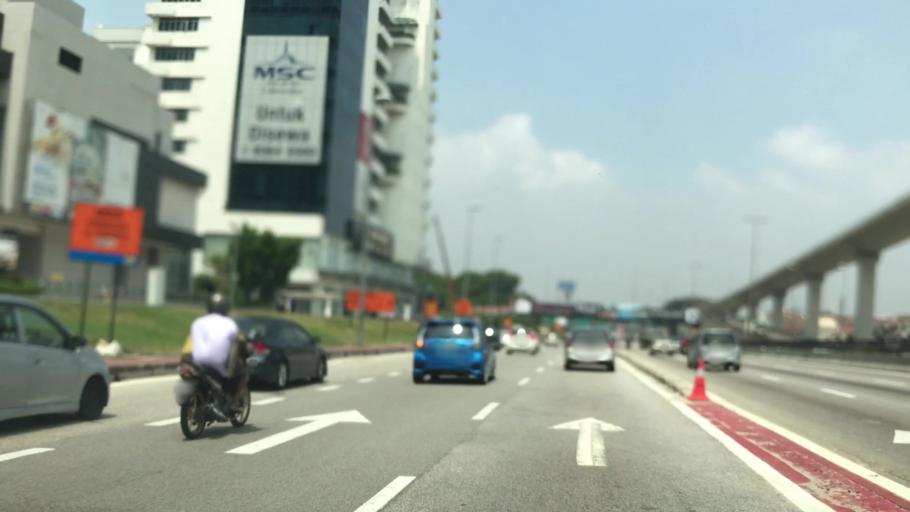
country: MY
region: Selangor
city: Subang Jaya
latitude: 3.0272
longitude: 101.6151
